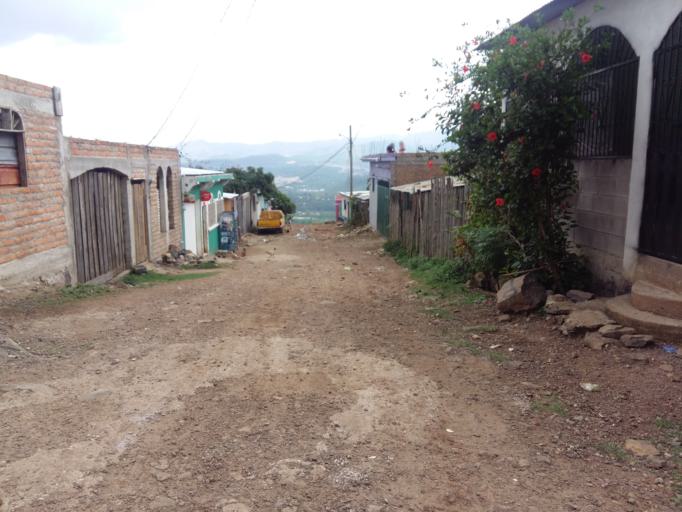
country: HN
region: Francisco Morazan
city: El Lolo
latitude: 14.0775
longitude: -87.2584
